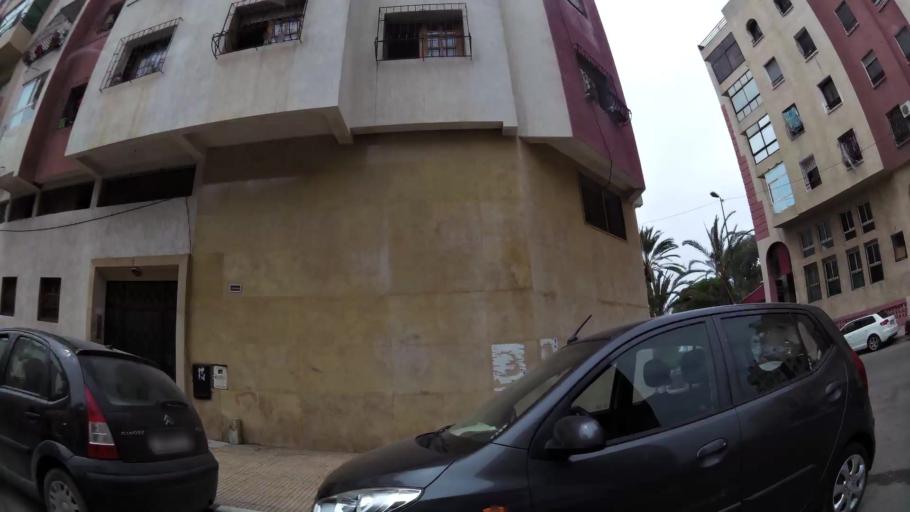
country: MA
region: Rabat-Sale-Zemmour-Zaer
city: Sale
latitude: 34.0344
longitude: -6.8021
